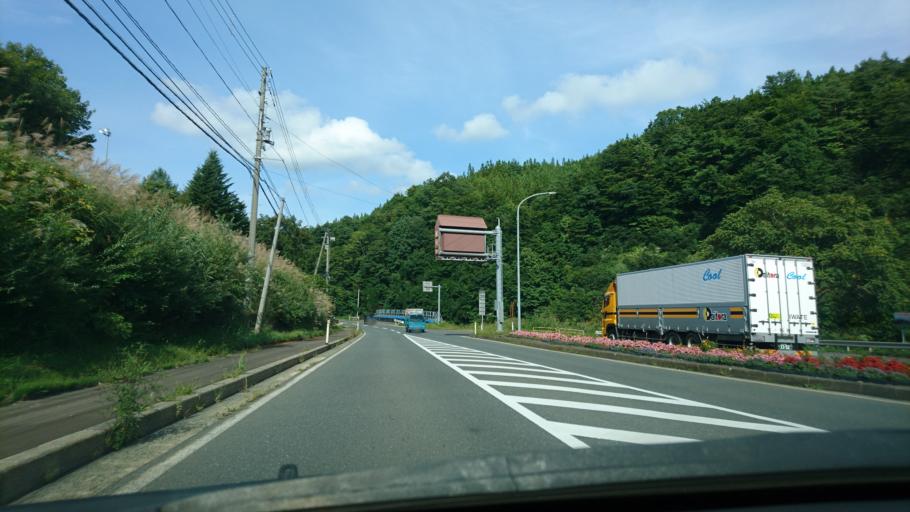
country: JP
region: Akita
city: Yokotemachi
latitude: 39.3114
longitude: 140.7490
